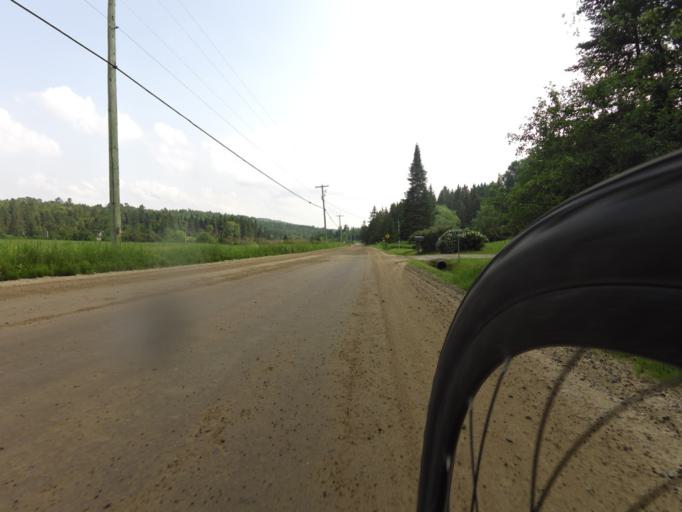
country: CA
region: Quebec
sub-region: Laurentides
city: Mont-Tremblant
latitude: 45.9474
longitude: -74.5944
